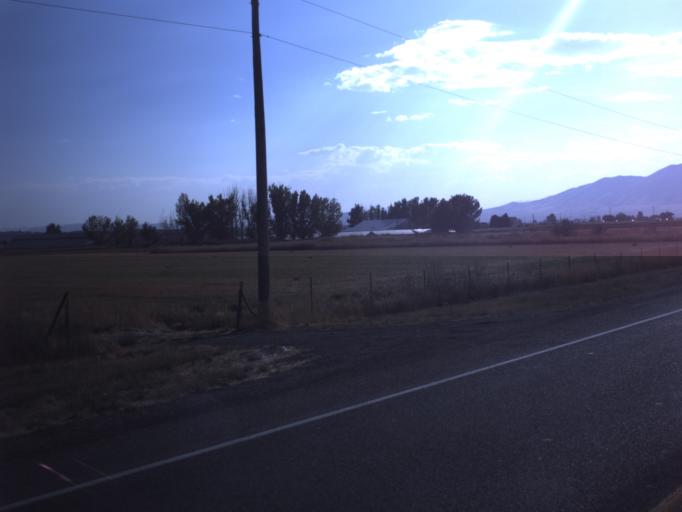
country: US
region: Utah
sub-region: Utah County
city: Salem
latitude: 40.0853
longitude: -111.6931
